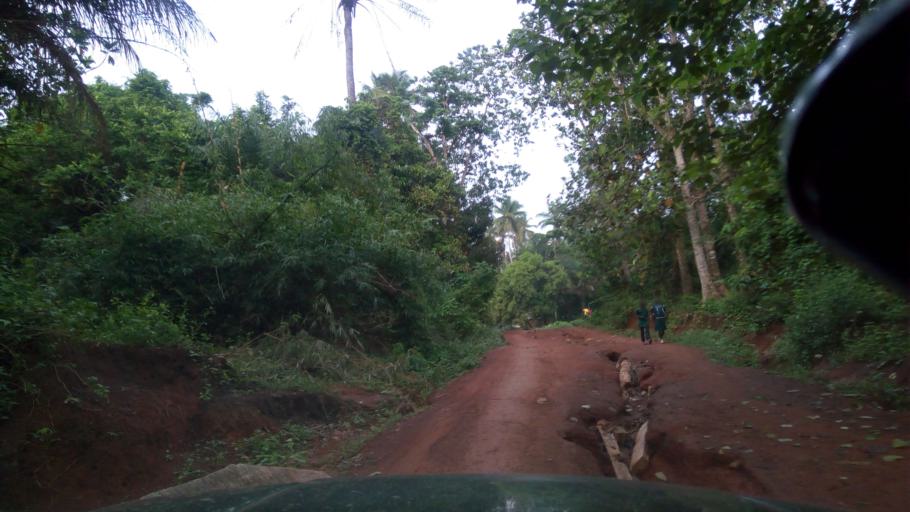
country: SL
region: Northern Province
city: Port Loko
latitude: 8.7441
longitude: -12.7924
